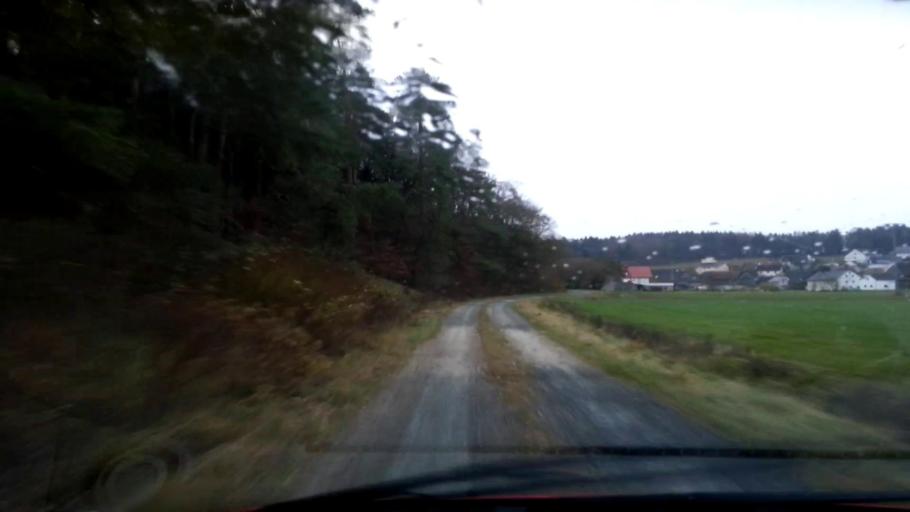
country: DE
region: Bavaria
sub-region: Upper Franconia
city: Aufsess
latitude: 49.9319
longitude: 11.2022
